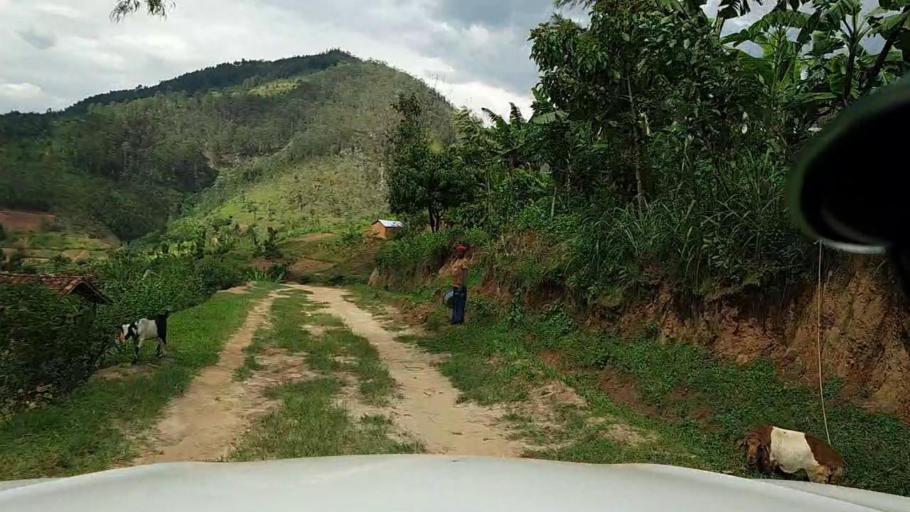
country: RW
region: Southern Province
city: Gitarama
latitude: -1.8181
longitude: 29.8007
